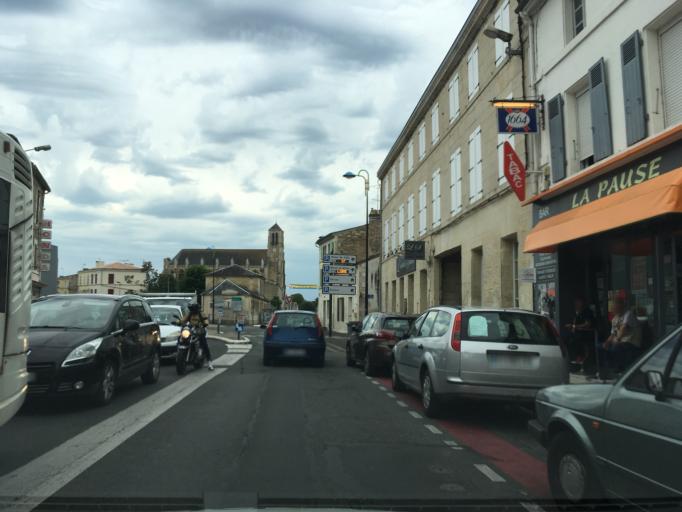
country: FR
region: Poitou-Charentes
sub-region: Departement des Deux-Sevres
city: Niort
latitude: 46.3301
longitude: -0.4701
